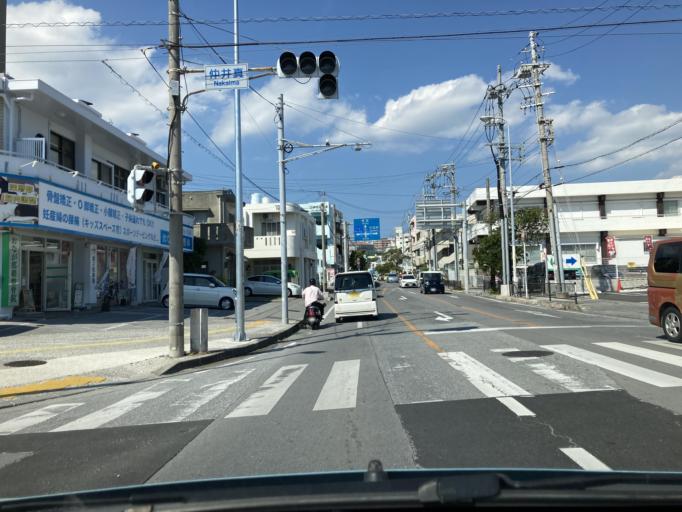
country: JP
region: Okinawa
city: Tomigusuku
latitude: 26.1927
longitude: 127.7070
